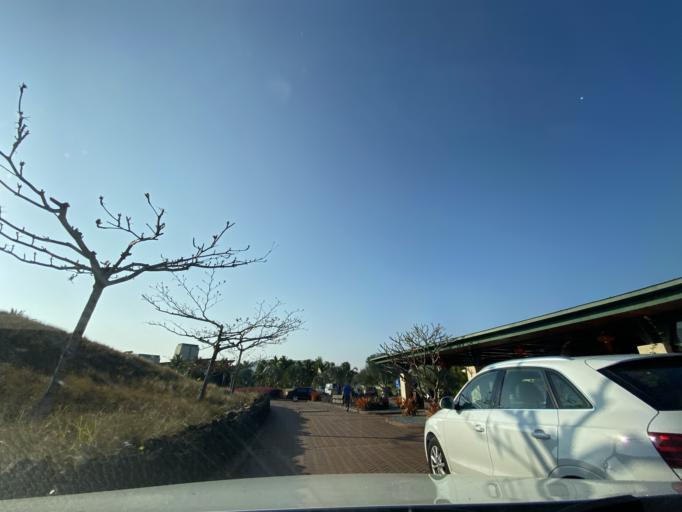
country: CN
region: Hainan
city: Xincun
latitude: 18.4184
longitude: 109.9533
